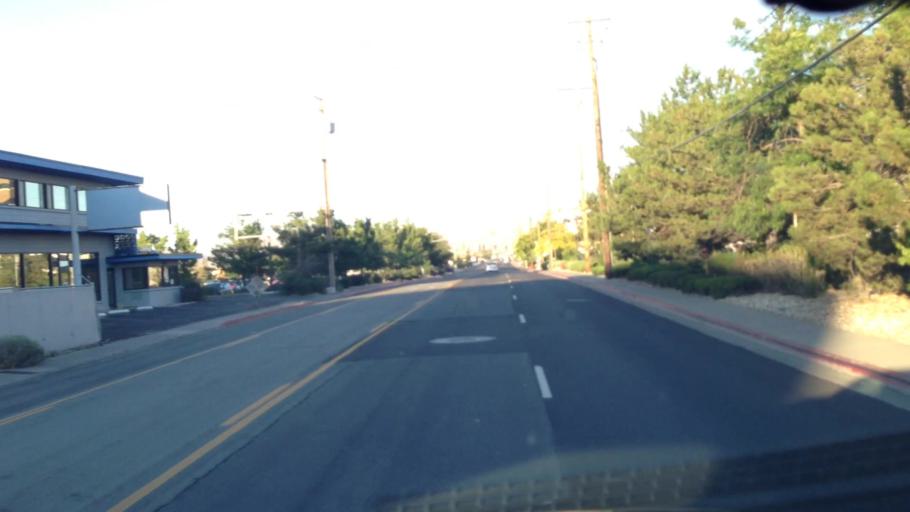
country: US
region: Nevada
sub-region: Washoe County
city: Reno
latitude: 39.5274
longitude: -119.7975
